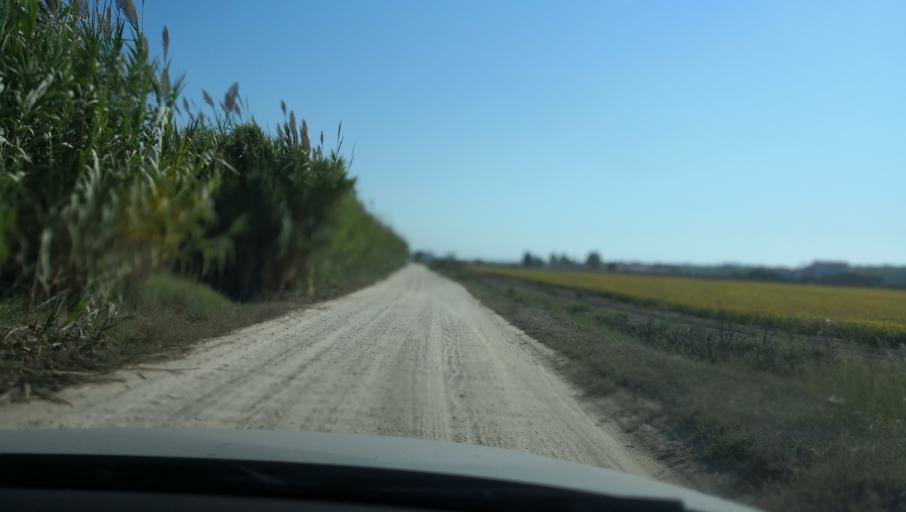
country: PT
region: Setubal
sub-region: Setubal
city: Setubal
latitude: 38.3857
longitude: -8.7892
